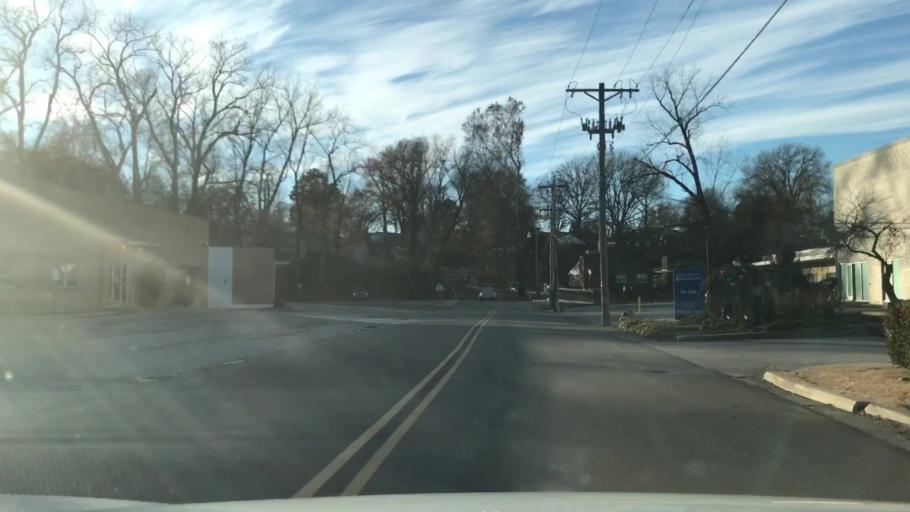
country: US
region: Missouri
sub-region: Saint Louis County
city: Maplewood
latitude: 38.6168
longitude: -90.3362
